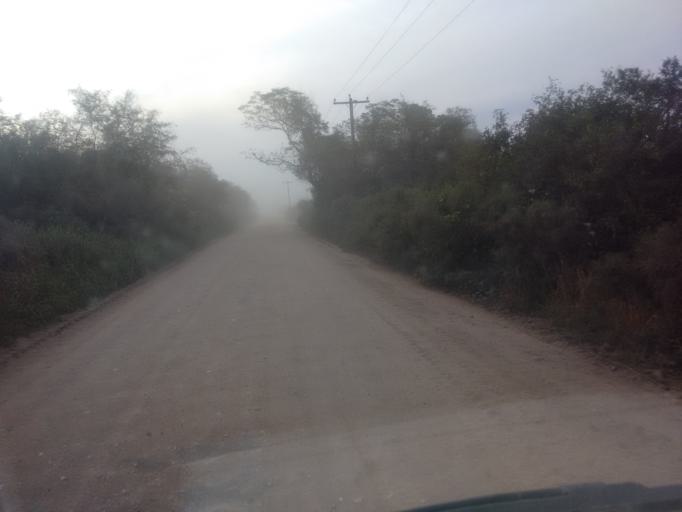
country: BR
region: Rio Grande do Sul
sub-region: Camaqua
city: Camaqua
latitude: -30.9307
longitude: -51.7900
